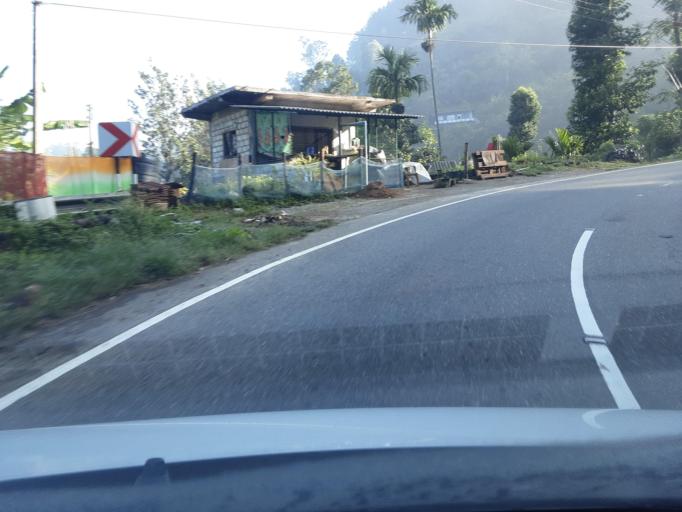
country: LK
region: Uva
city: Badulla
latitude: 6.9205
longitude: 80.9640
